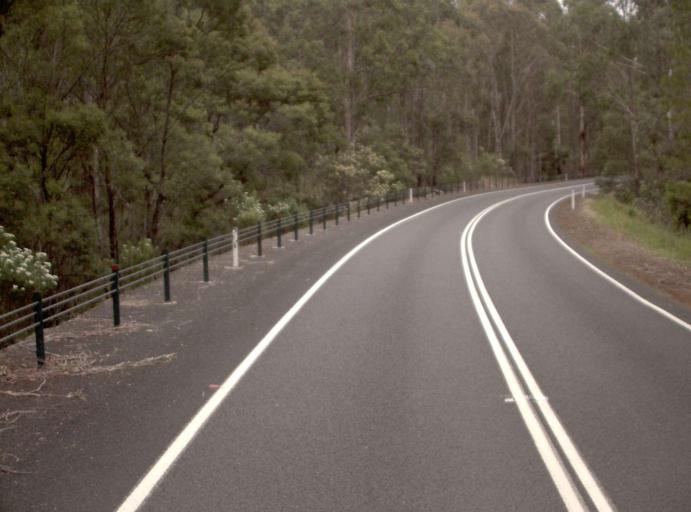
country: AU
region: New South Wales
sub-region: Bombala
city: Bombala
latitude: -37.3546
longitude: 149.2023
